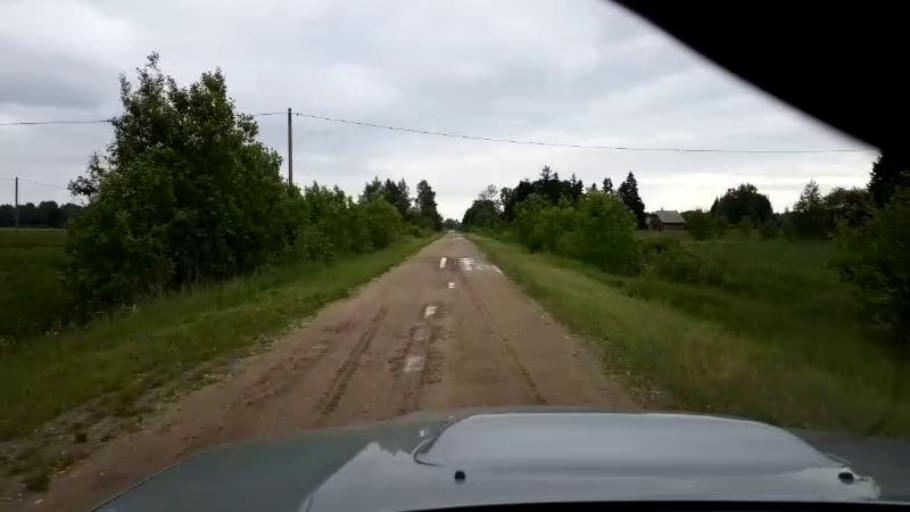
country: EE
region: Paernumaa
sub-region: Halinga vald
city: Parnu-Jaagupi
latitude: 58.5585
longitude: 24.5757
